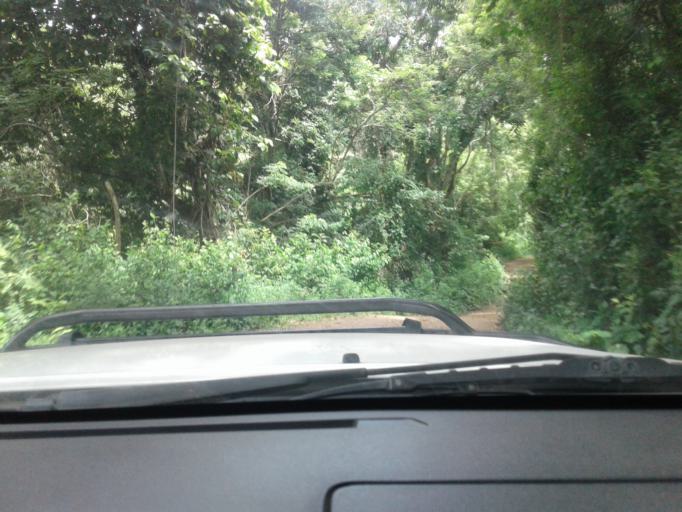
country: NI
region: Matagalpa
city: San Ramon
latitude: 12.9195
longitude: -85.7307
